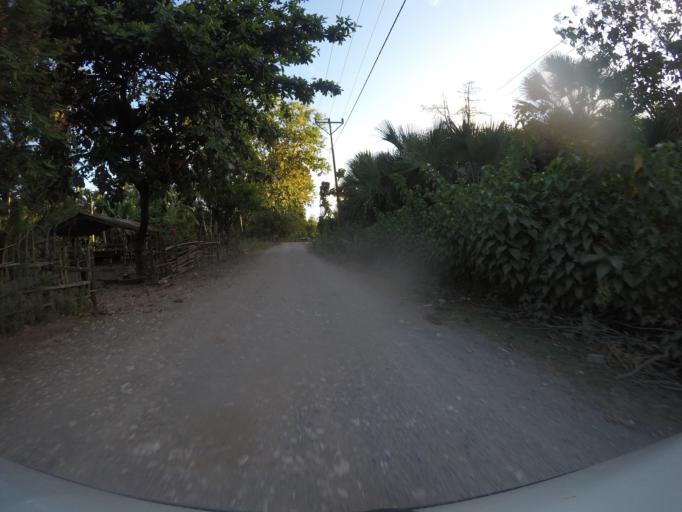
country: TL
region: Baucau
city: Venilale
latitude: -8.7440
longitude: 126.7140
